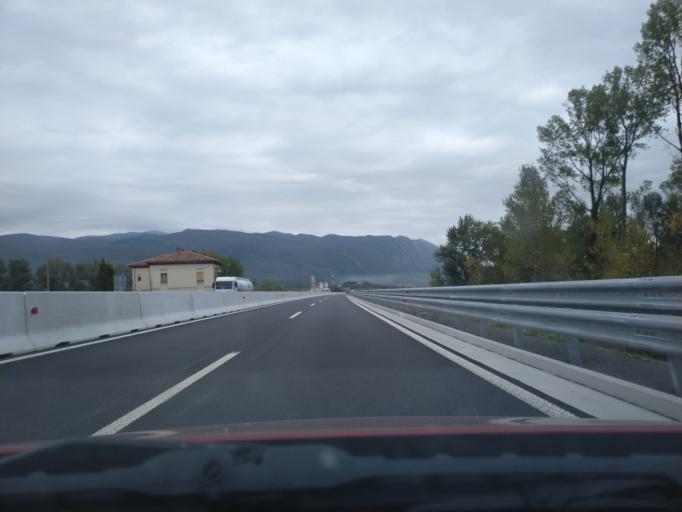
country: SI
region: Ajdovscina
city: Ajdovscina
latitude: 45.8711
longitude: 13.9261
